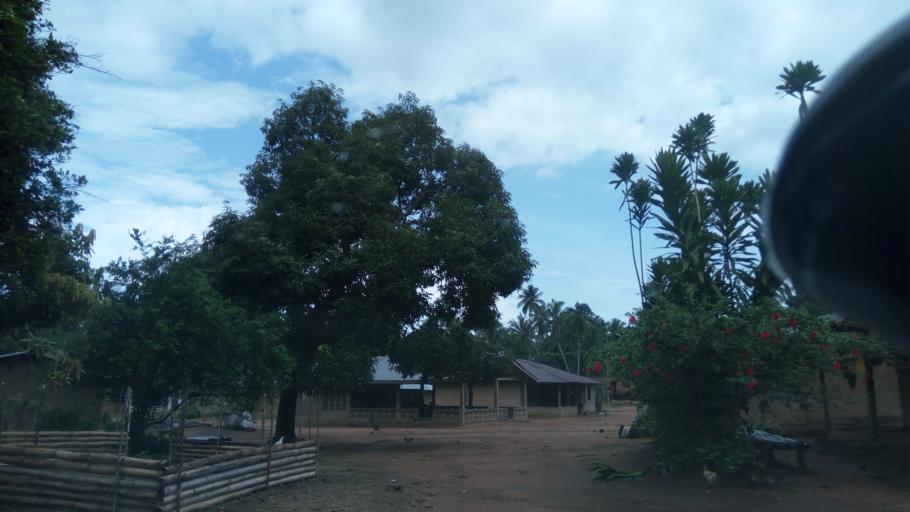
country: LR
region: Grand Cape Mount
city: Robertsport
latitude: 6.9329
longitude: -11.4796
